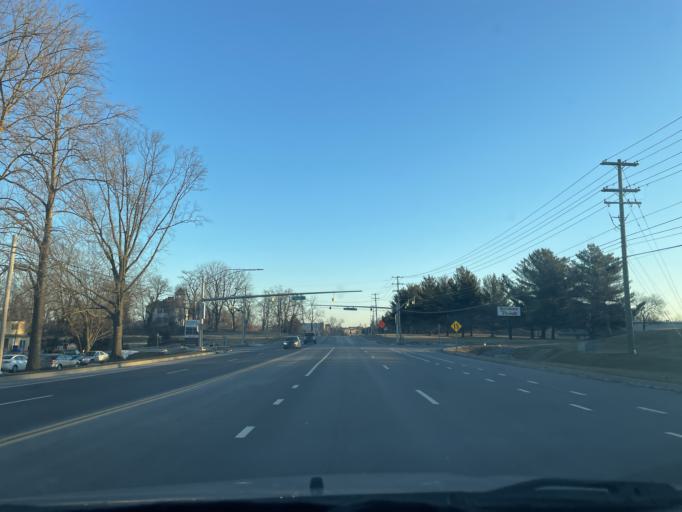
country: US
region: Maryland
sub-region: Frederick County
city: Ballenger Creek
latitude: 39.3610
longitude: -77.4189
